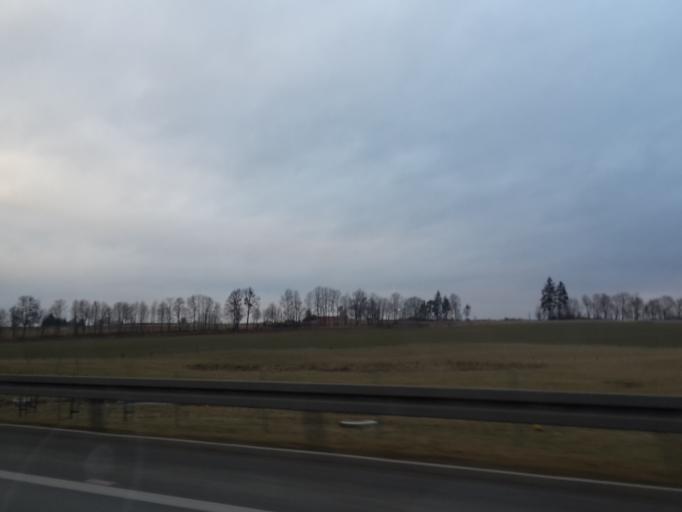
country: PL
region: Warmian-Masurian Voivodeship
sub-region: Powiat ostrodzki
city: Milomlyn
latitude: 53.8014
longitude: 19.7916
